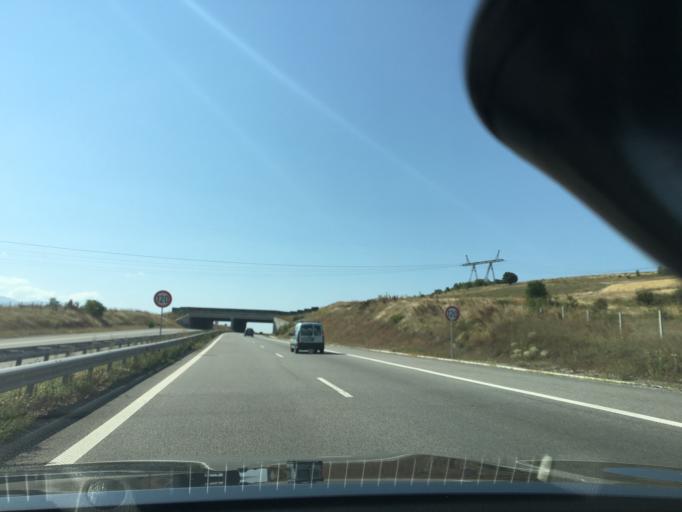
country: BG
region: Kyustendil
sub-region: Obshtina Bobovdol
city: Bobovdol
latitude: 42.3798
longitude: 23.1126
